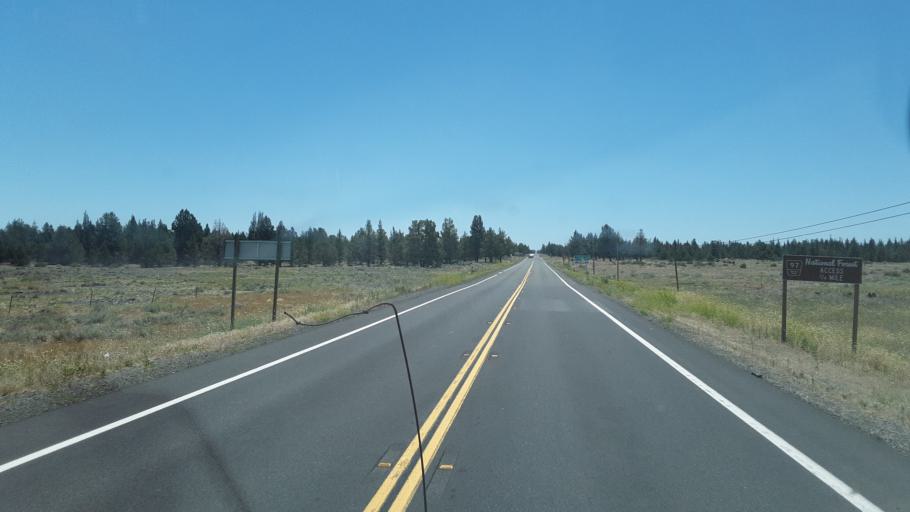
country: US
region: California
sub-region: Siskiyou County
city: Tulelake
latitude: 41.6732
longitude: -121.2591
